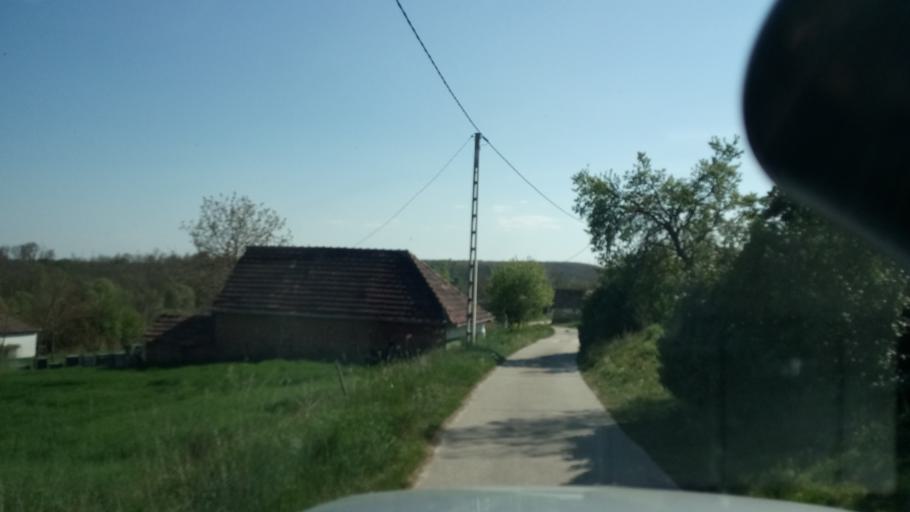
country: HU
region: Zala
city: Sarmellek
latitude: 46.6999
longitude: 17.1008
